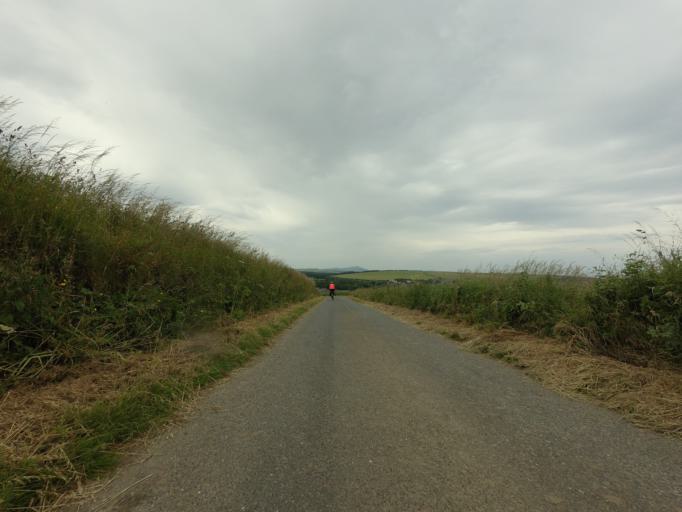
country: GB
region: Scotland
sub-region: Aberdeenshire
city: Portsoy
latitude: 57.6790
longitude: -2.6783
